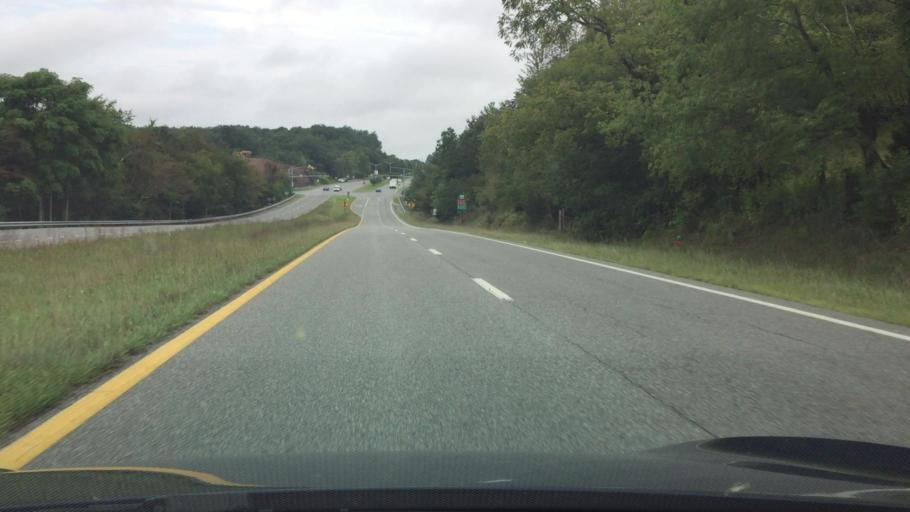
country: US
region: Virginia
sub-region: City of Radford
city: Radford
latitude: 37.1169
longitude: -80.5298
